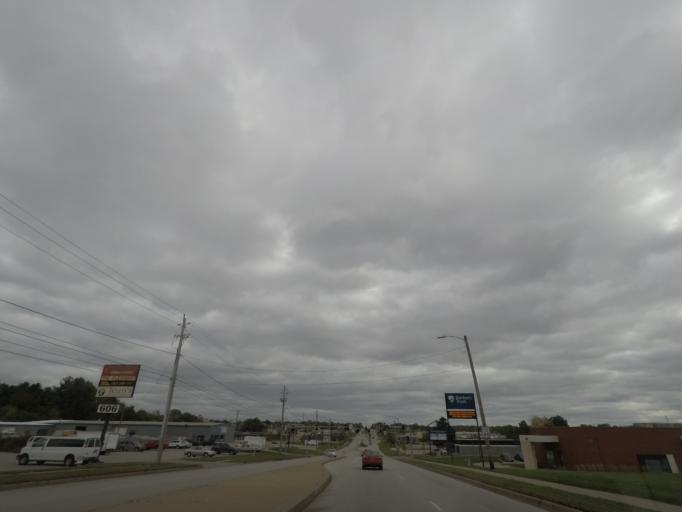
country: US
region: Iowa
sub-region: Polk County
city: Des Moines
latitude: 41.5263
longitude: -93.6051
